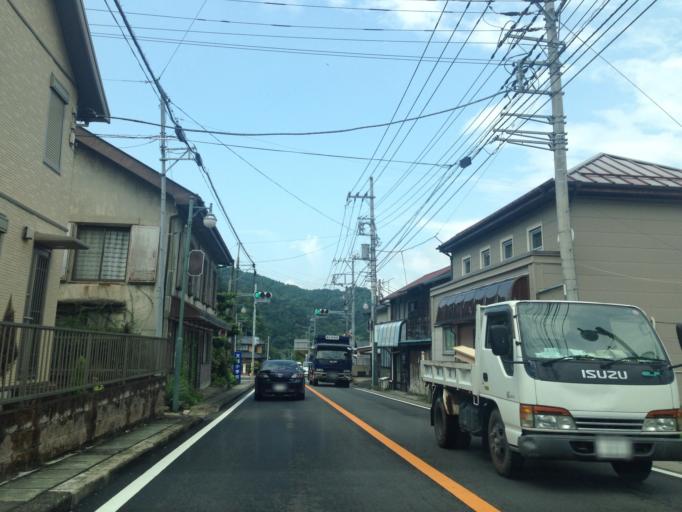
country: JP
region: Shizuoka
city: Heda
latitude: 34.9364
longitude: 138.9317
